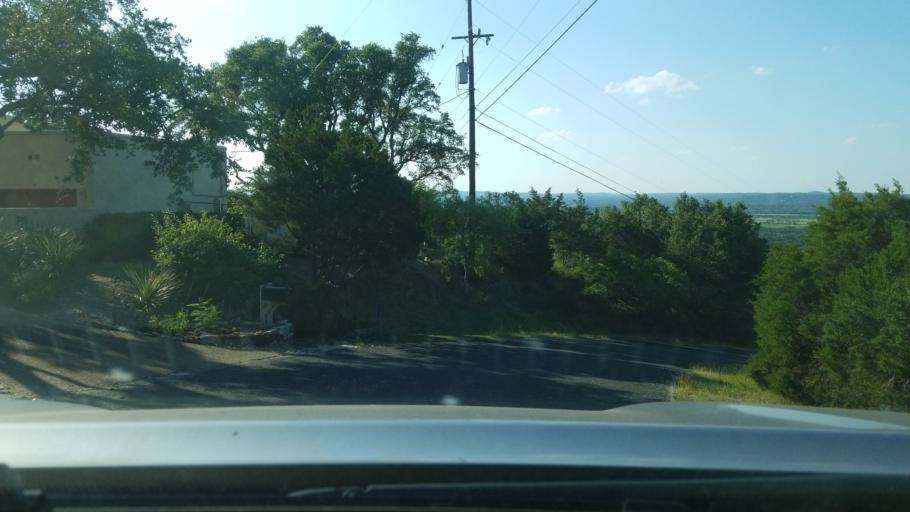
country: US
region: Texas
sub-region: Bexar County
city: Timberwood Park
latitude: 29.7088
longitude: -98.4457
